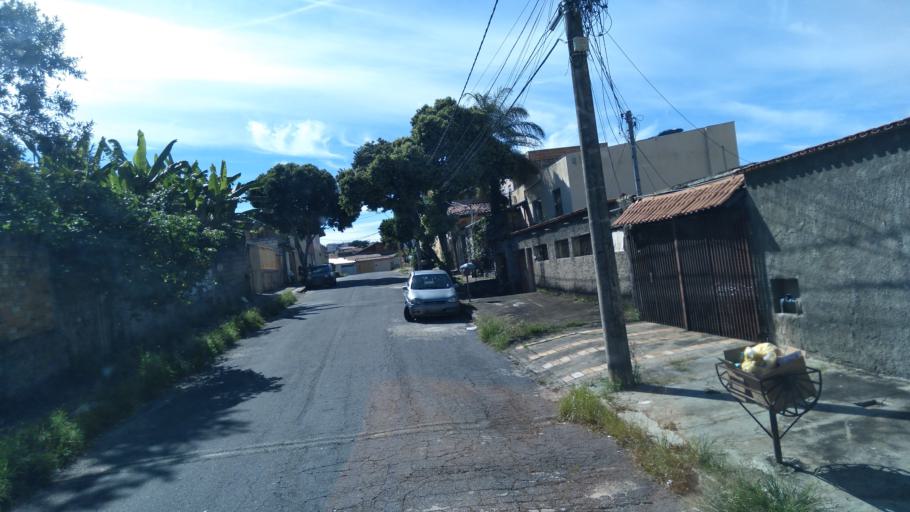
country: BR
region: Minas Gerais
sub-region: Contagem
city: Contagem
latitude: -19.9057
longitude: -44.0043
